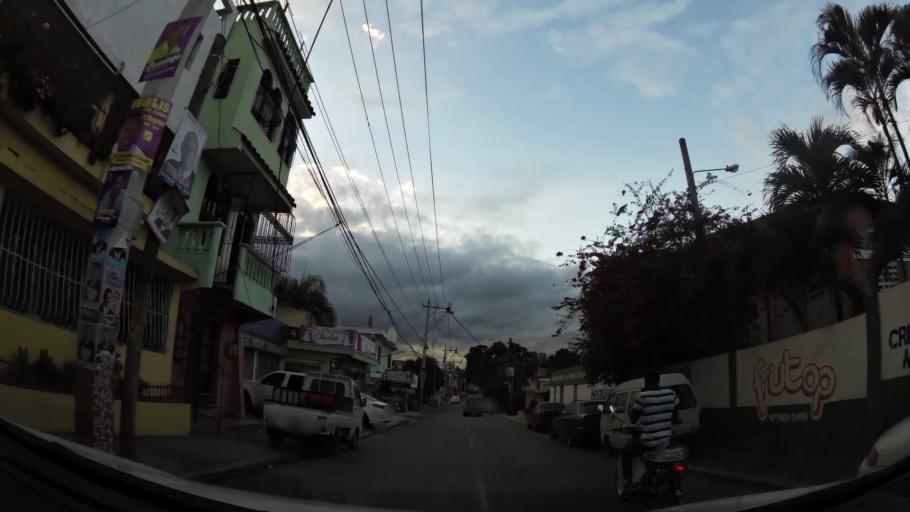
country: DO
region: Santo Domingo
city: Santo Domingo Oeste
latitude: 18.5229
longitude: -70.0141
